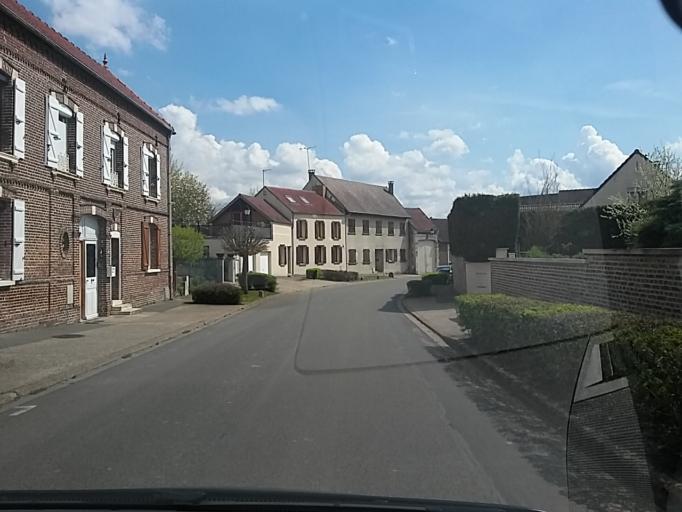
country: FR
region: Picardie
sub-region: Departement de l'Oise
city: Grandfresnoy
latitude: 49.3667
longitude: 2.6593
